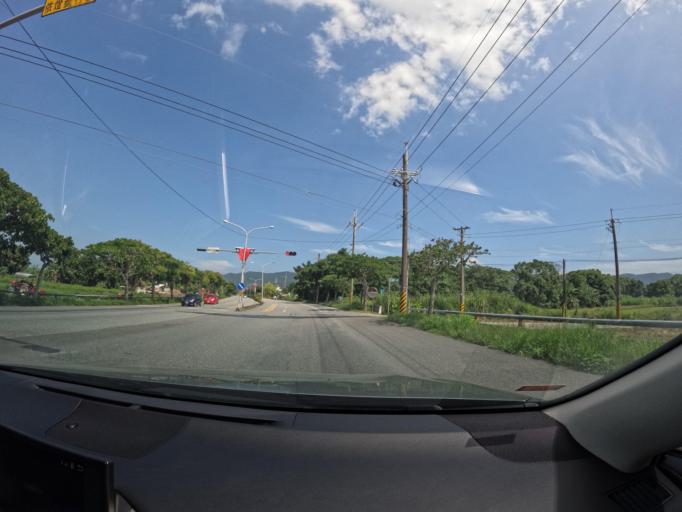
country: TW
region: Taiwan
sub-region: Hualien
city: Hualian
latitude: 23.8147
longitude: 121.4794
